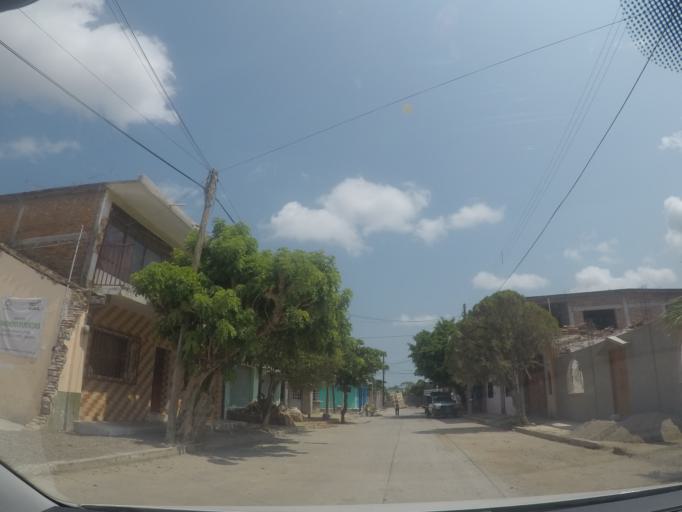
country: MX
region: Oaxaca
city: Asuncion Ixtaltepec
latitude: 16.5044
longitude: -95.0554
